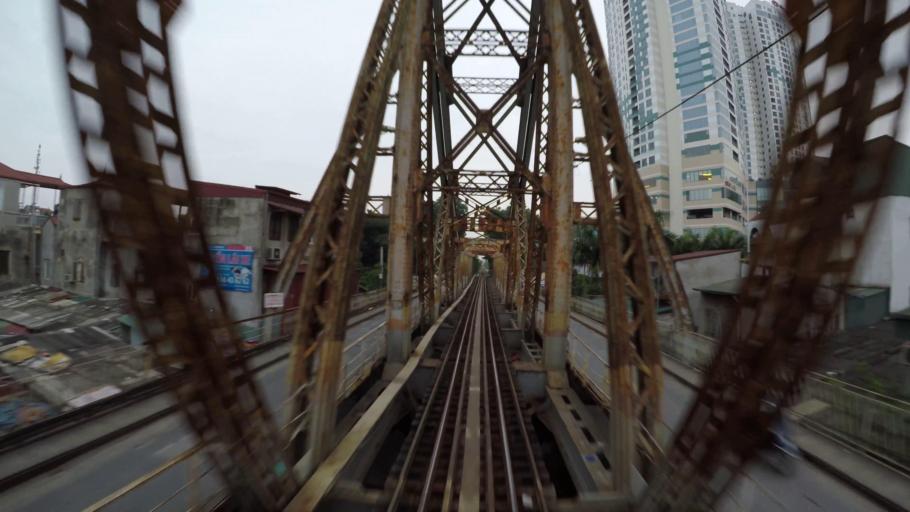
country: VN
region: Ha Noi
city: Hoan Kiem
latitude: 21.0509
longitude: 105.8910
